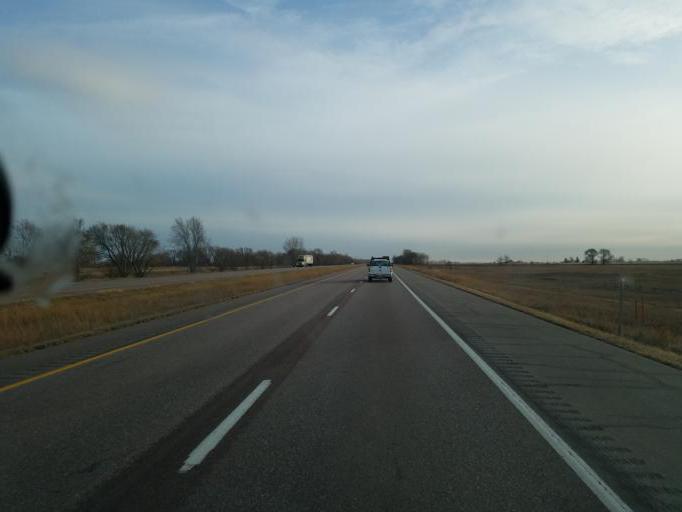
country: US
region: Nebraska
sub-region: Thurston County
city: Macy
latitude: 42.1539
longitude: -96.2217
